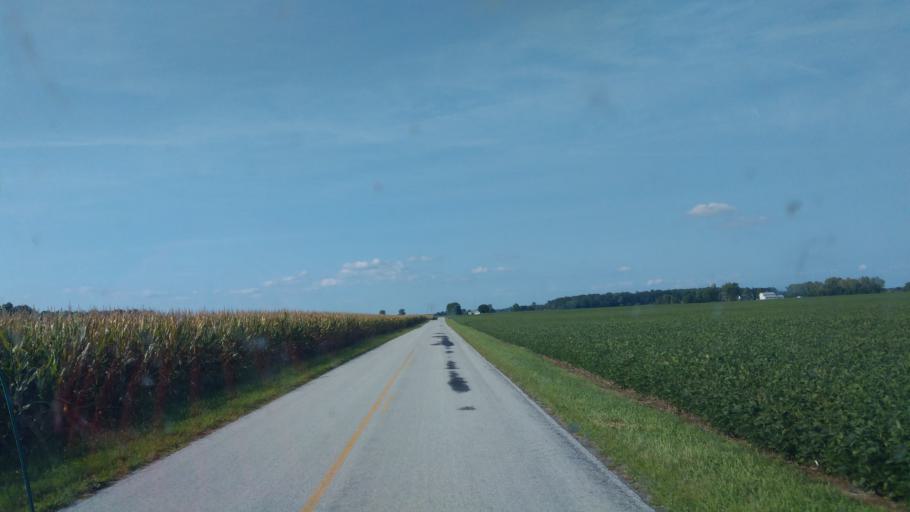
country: US
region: Ohio
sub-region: Hardin County
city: Kenton
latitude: 40.7176
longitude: -83.5725
